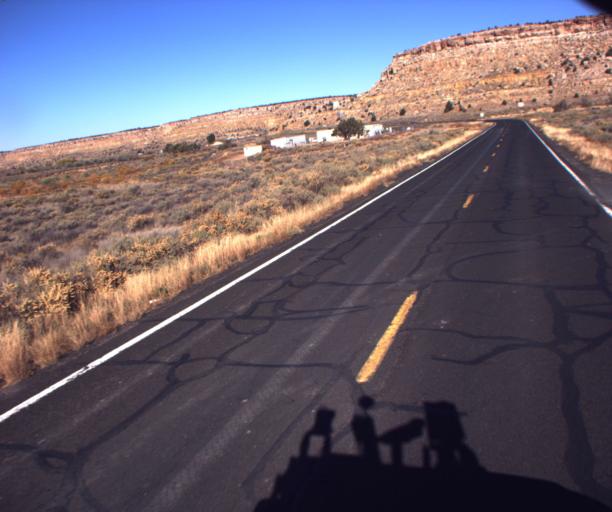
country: US
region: Arizona
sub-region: Navajo County
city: First Mesa
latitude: 35.8362
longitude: -110.2299
